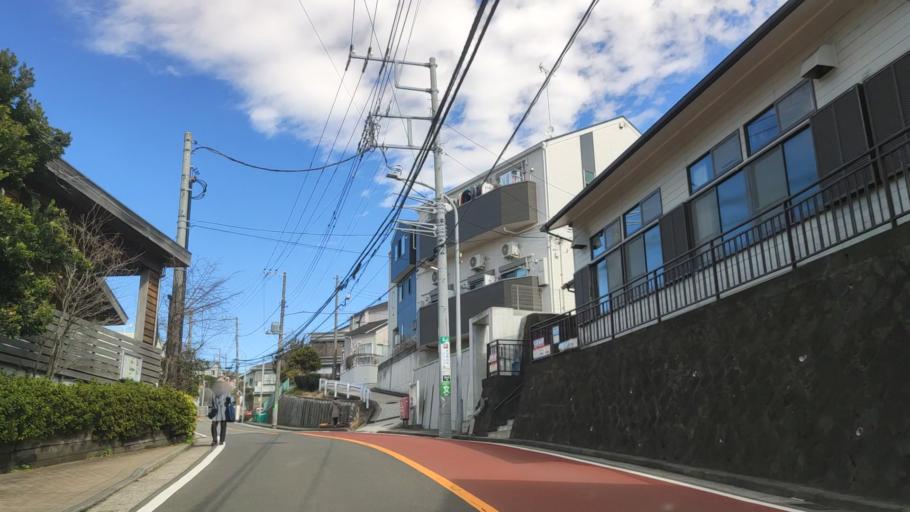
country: JP
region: Kanagawa
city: Yokohama
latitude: 35.4681
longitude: 139.5846
